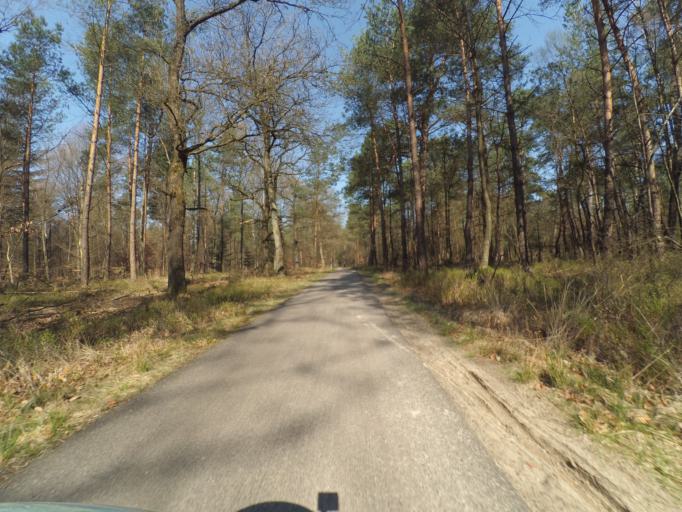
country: NL
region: Gelderland
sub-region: Gemeente Ede
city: Otterlo
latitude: 52.1017
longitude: 5.8565
